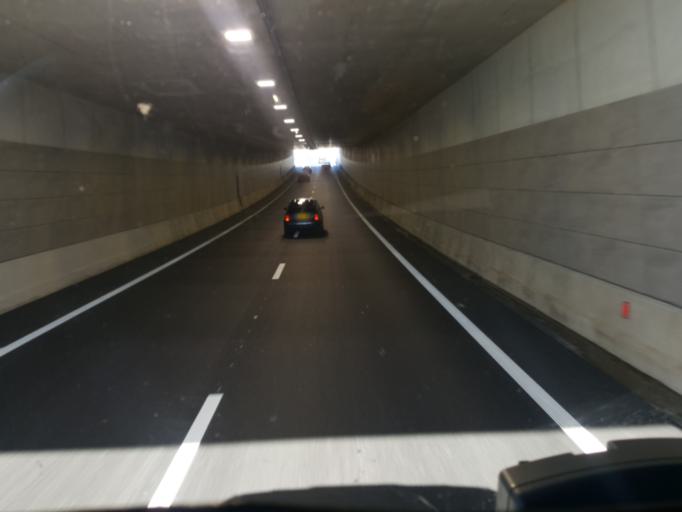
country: NL
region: North Holland
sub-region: Gemeente Medemblik
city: Medemblik
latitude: 52.6901
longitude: 5.1595
